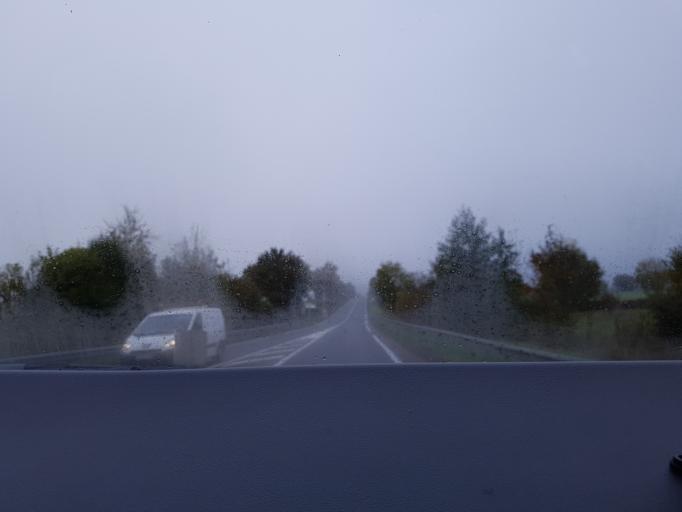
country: FR
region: Poitou-Charentes
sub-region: Departement des Deux-Sevres
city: Viennay
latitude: 46.7082
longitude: -0.2866
